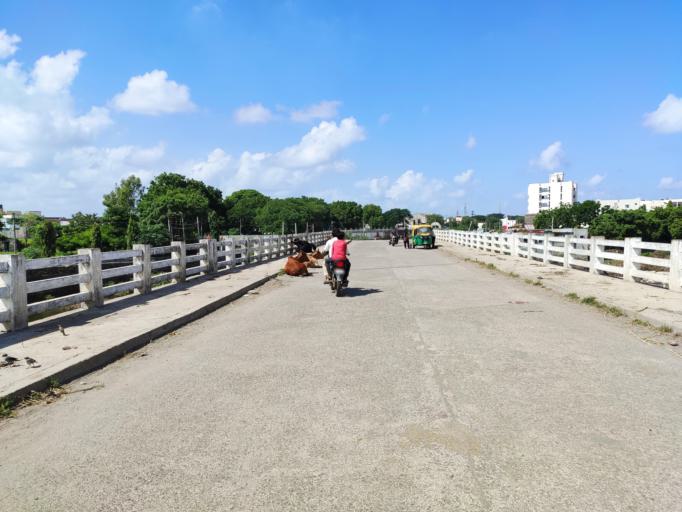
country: IN
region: Gujarat
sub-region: Jamnagar
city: Jamnagar
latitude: 22.4586
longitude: 70.0938
